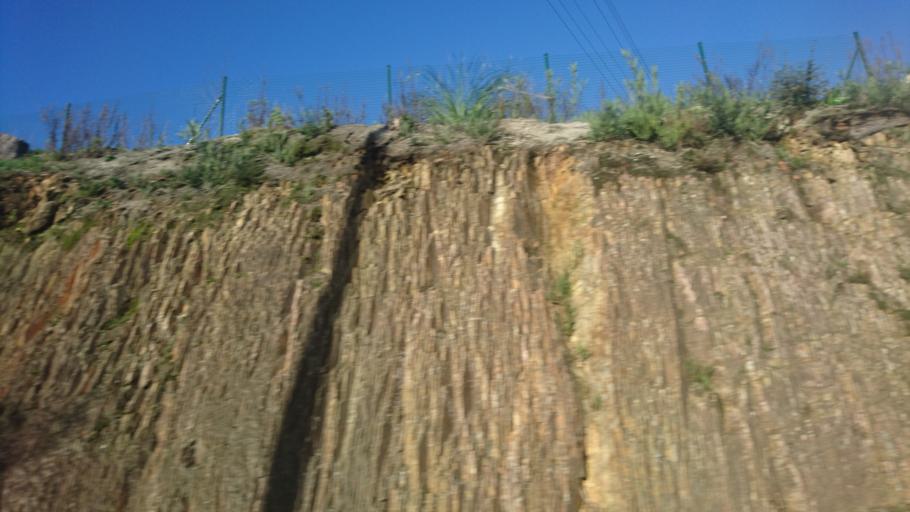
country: PT
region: Porto
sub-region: Paredes
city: Recarei
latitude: 41.1636
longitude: -8.4319
